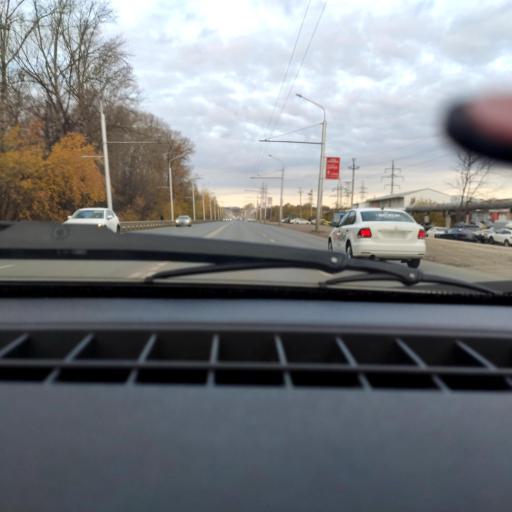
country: RU
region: Bashkortostan
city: Ufa
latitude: 54.7901
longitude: 56.1001
